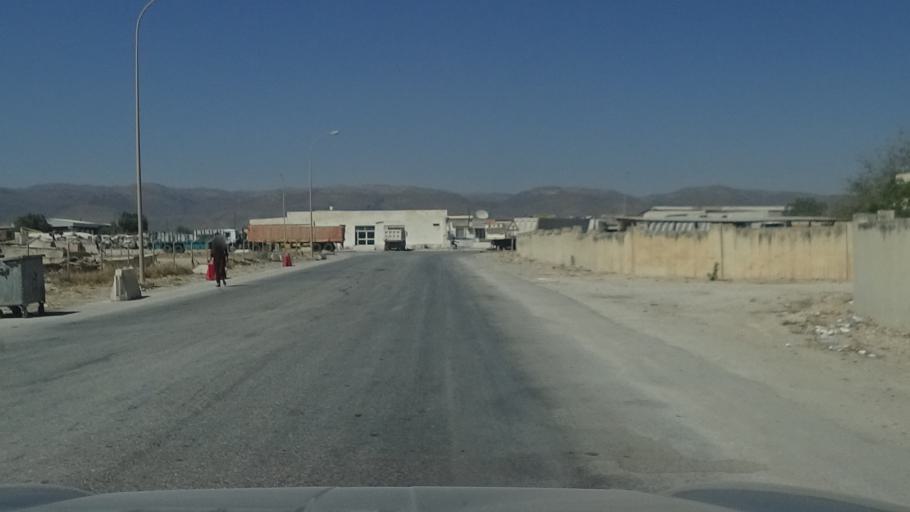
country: OM
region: Zufar
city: Salalah
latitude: 17.0273
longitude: 54.0437
